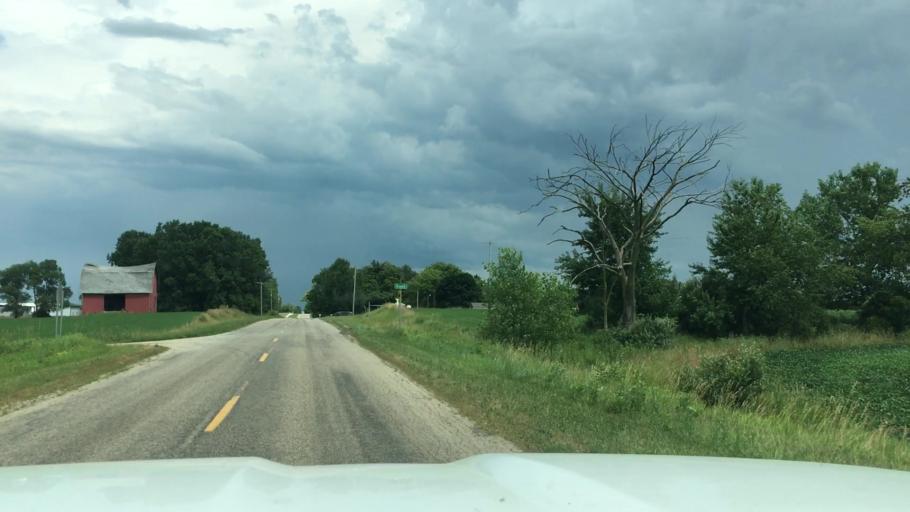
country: US
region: Michigan
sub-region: Montcalm County
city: Carson City
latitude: 43.2486
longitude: -84.7681
